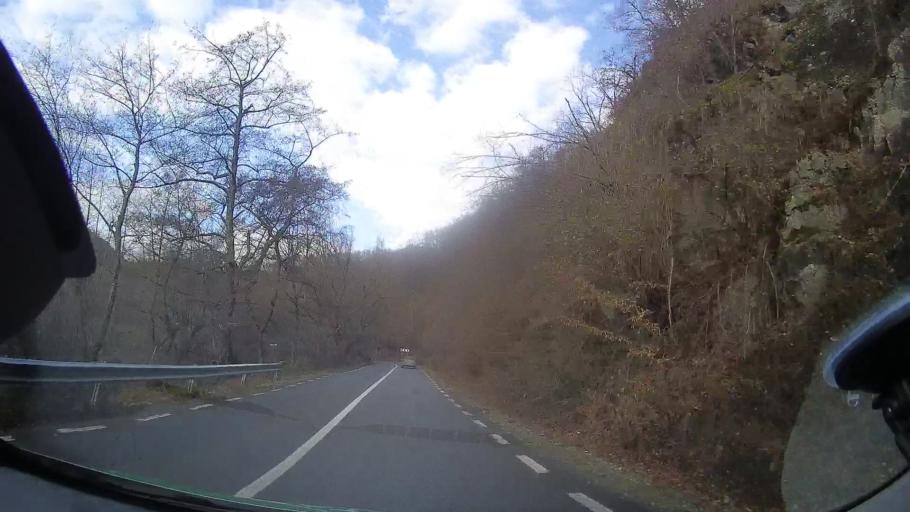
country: RO
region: Cluj
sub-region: Comuna Baisoara
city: Baisoara
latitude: 46.6042
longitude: 23.4245
